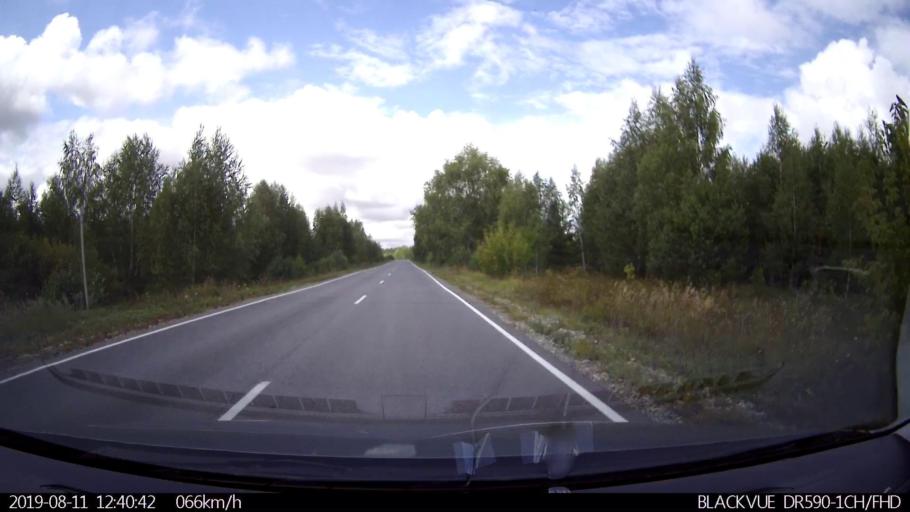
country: RU
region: Ulyanovsk
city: Ignatovka
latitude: 53.8401
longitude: 47.7770
